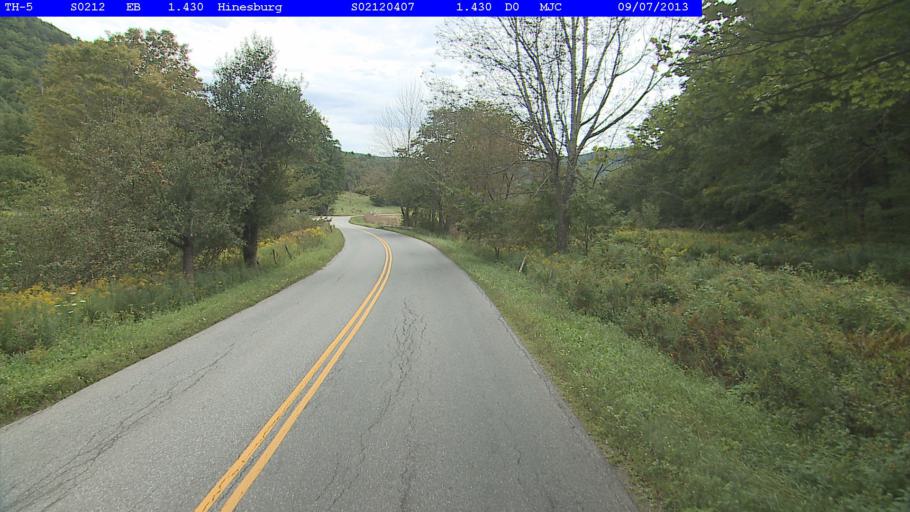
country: US
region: Vermont
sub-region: Chittenden County
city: Hinesburg
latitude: 44.2916
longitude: -73.0425
